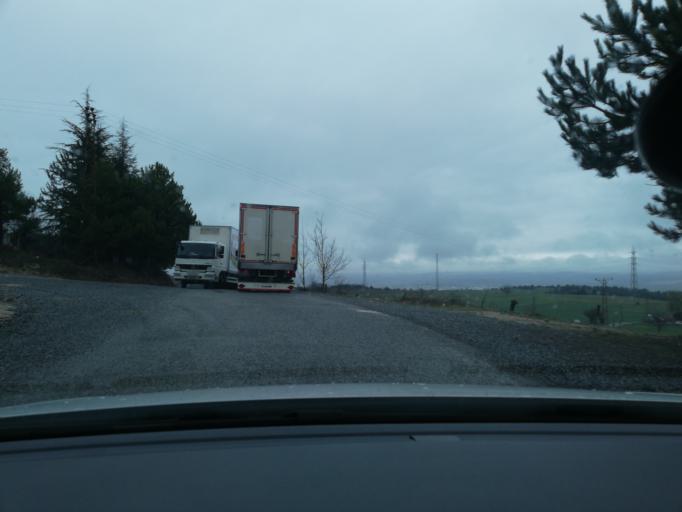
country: TR
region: Bolu
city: Bolu
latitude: 40.7722
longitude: 31.6504
